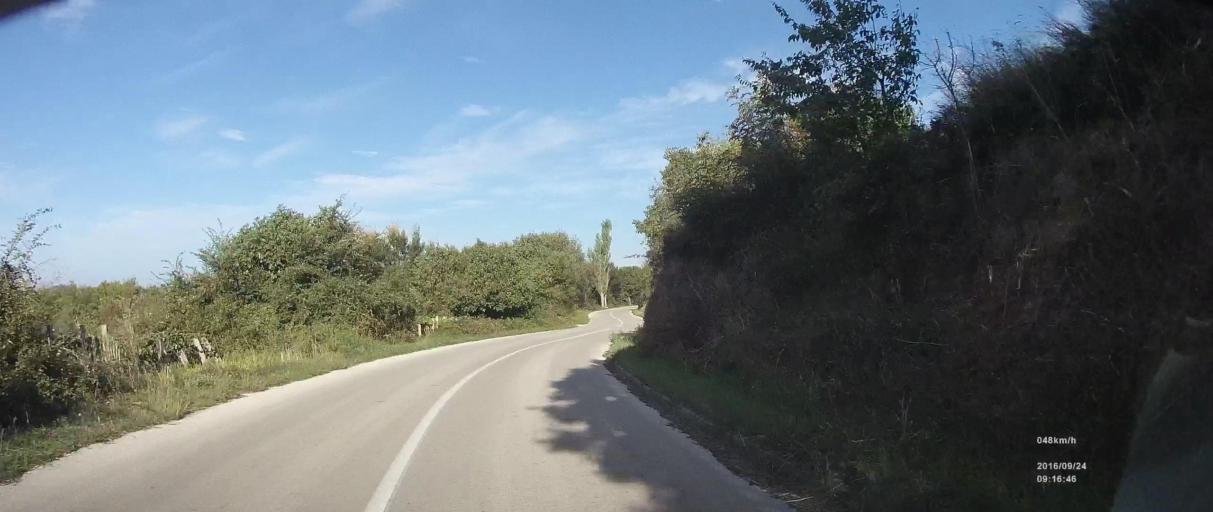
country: HR
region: Zadarska
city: Polaca
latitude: 44.0484
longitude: 15.5268
